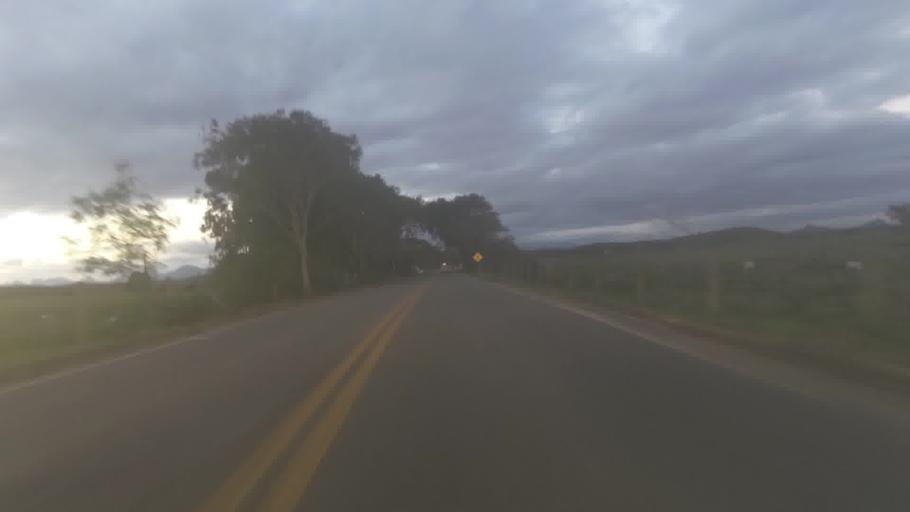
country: BR
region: Espirito Santo
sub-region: Itapemirim
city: Itapemirim
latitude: -20.9841
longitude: -40.8646
